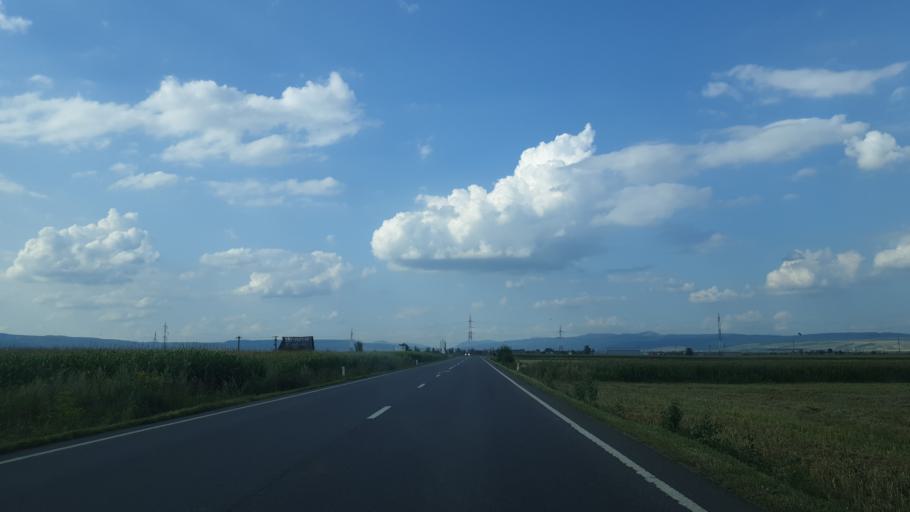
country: RO
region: Covasna
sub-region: Comuna Chichis
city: Chichis
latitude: 45.8217
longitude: 25.7997
